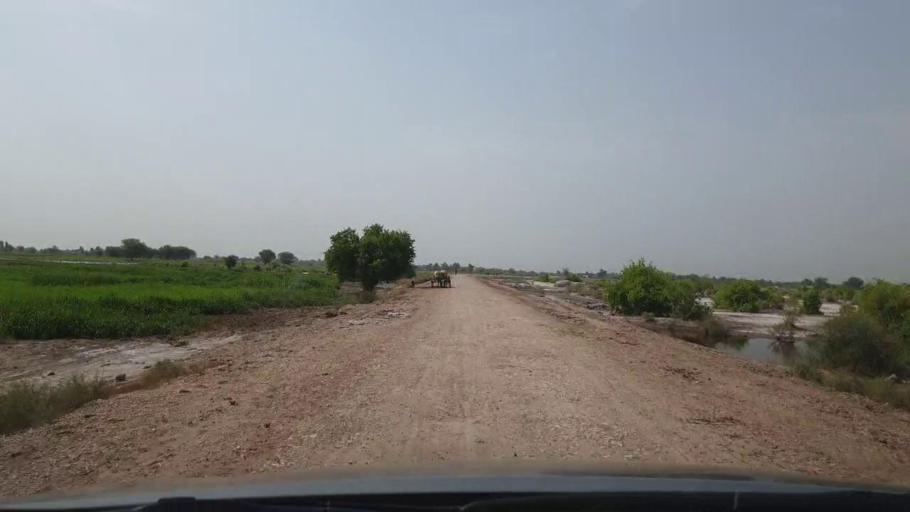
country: PK
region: Sindh
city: Rohri
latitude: 27.6708
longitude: 69.0133
